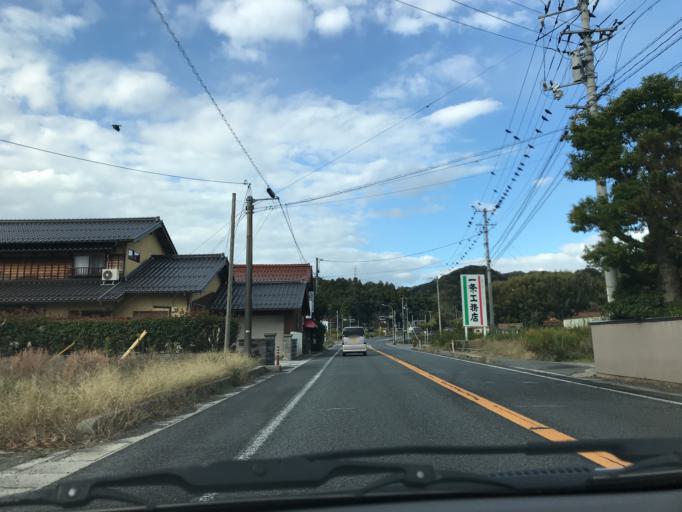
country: JP
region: Tottori
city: Yonago
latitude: 35.4081
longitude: 133.3010
